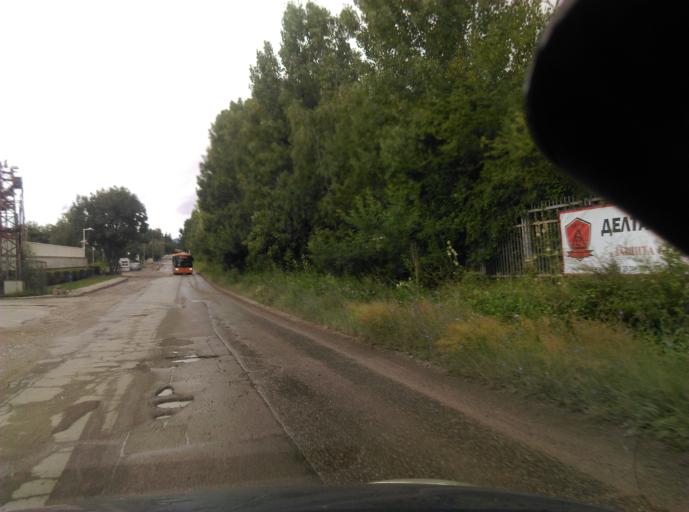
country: BG
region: Sofia-Capital
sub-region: Stolichna Obshtina
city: Sofia
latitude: 42.6400
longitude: 23.2950
